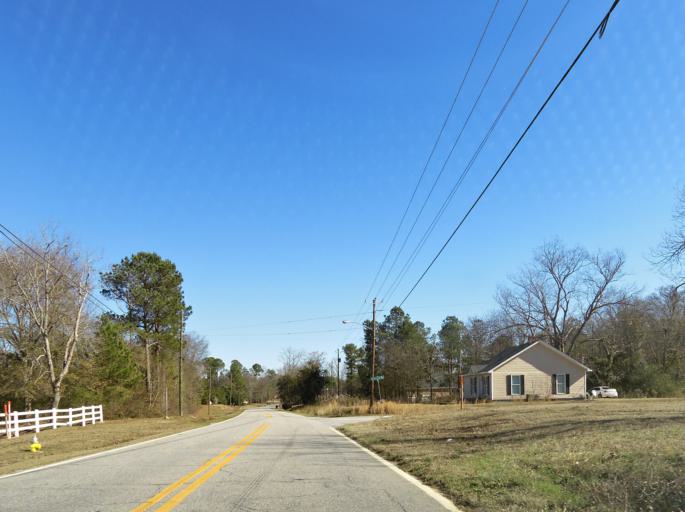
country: US
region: Georgia
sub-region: Bibb County
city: West Point
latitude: 32.8076
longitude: -83.7845
